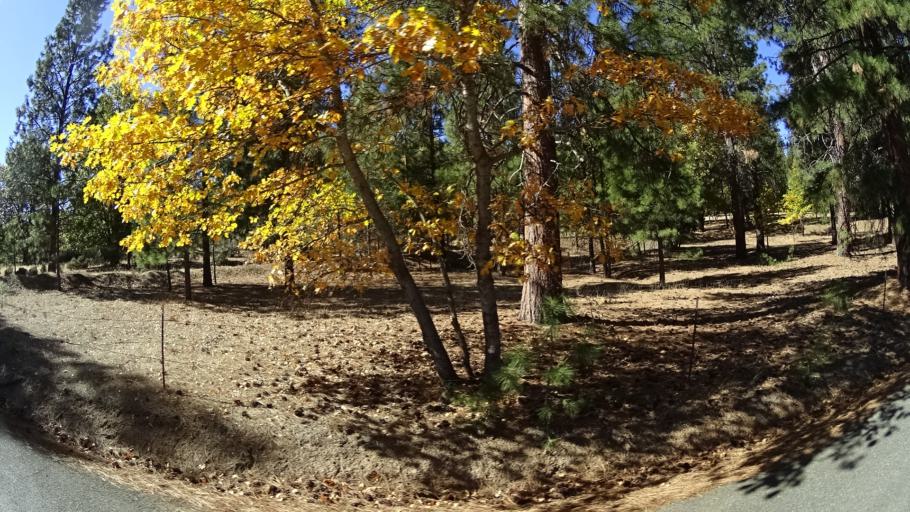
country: US
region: California
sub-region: Siskiyou County
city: Yreka
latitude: 41.5972
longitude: -122.9111
